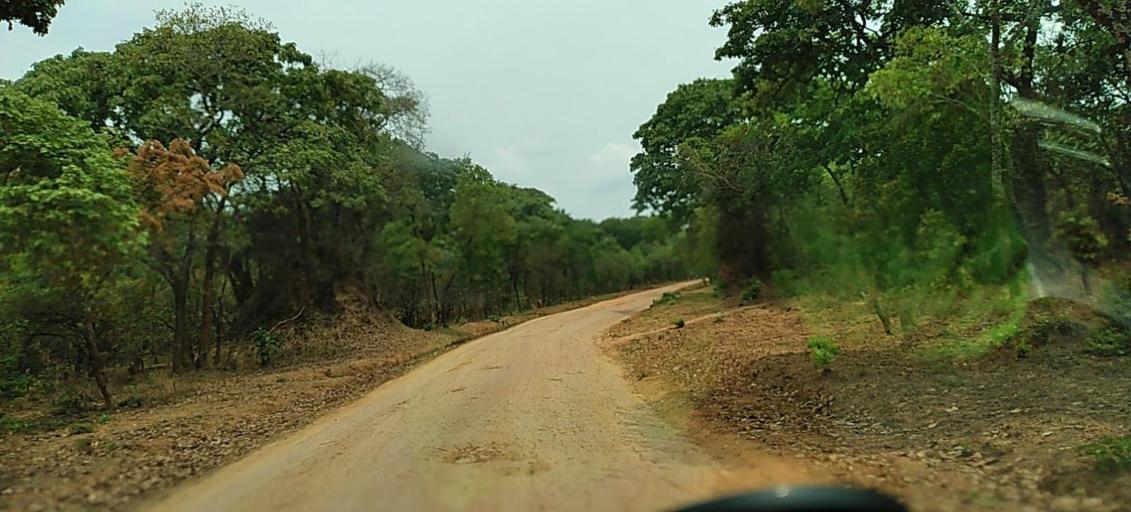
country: ZM
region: North-Western
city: Solwezi
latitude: -12.8263
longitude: 26.5374
